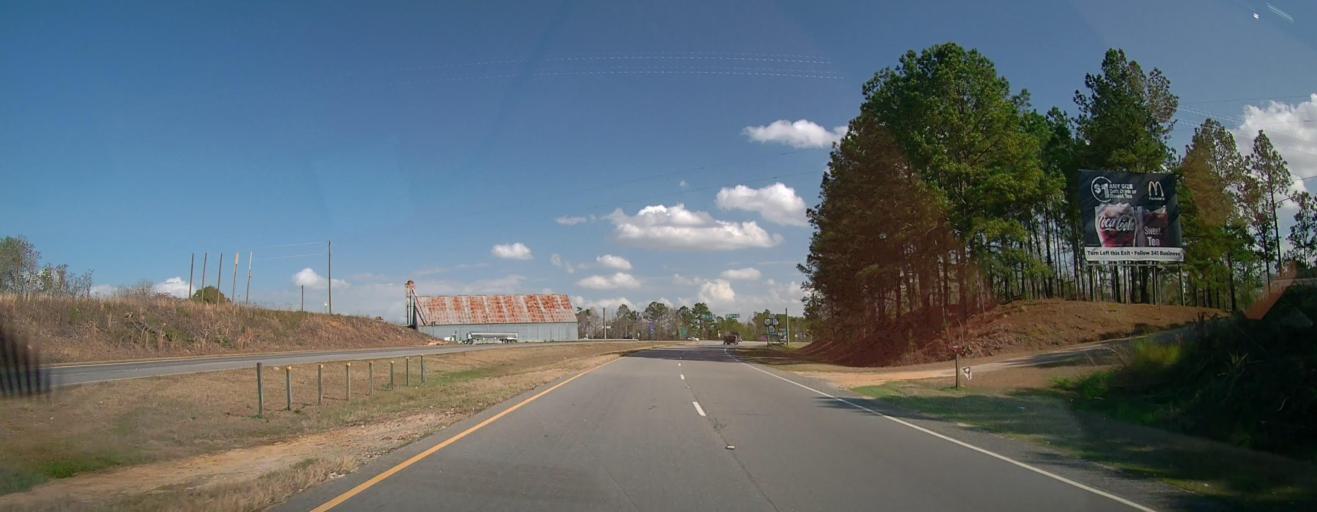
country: US
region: Georgia
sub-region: Dodge County
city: Eastman
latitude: 32.1968
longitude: -83.2121
